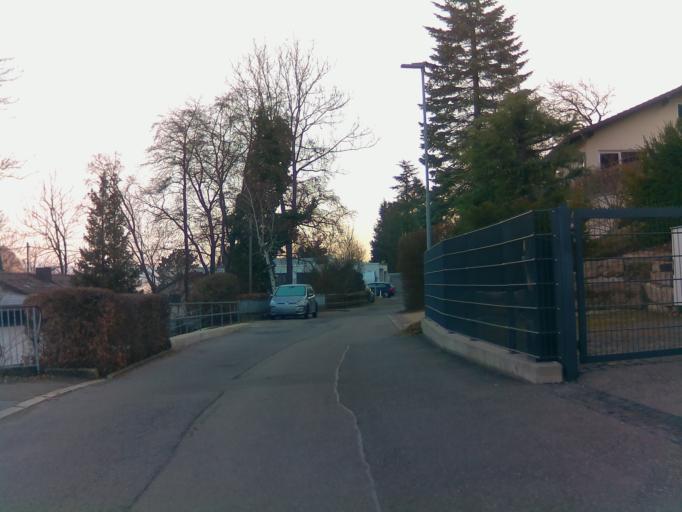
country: DE
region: Baden-Wuerttemberg
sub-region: Karlsruhe Region
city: Mosbach
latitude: 49.3445
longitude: 9.1381
